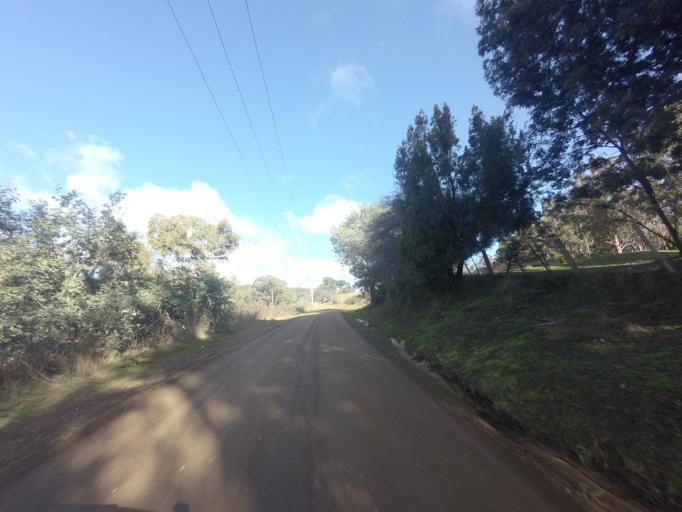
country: AU
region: Tasmania
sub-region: Derwent Valley
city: New Norfolk
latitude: -42.8204
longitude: 147.1223
